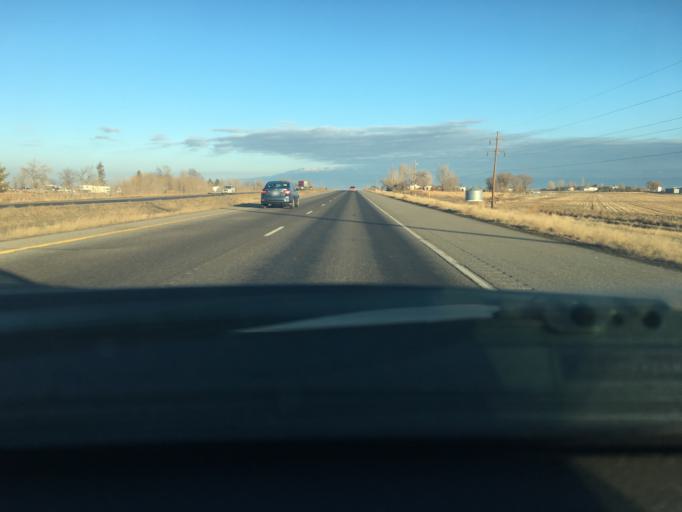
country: US
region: Colorado
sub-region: Montrose County
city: Olathe
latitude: 38.5673
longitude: -107.9576
